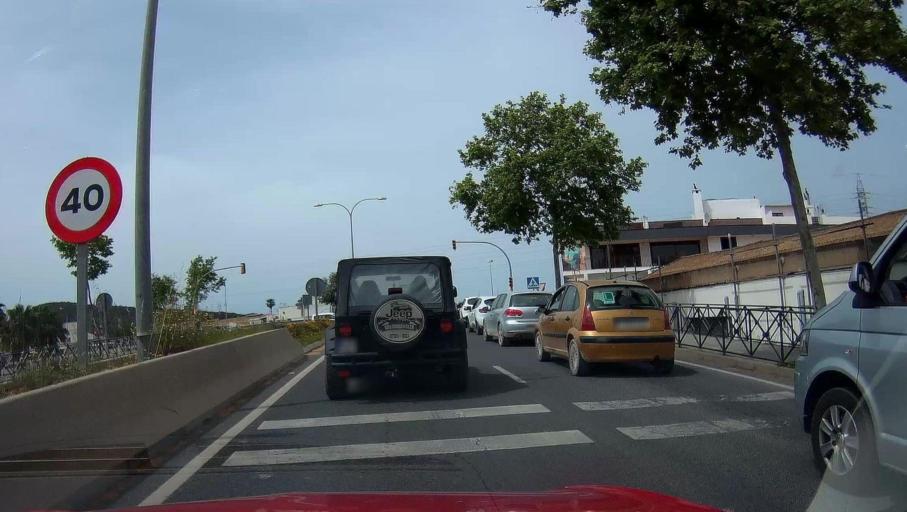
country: ES
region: Balearic Islands
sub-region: Illes Balears
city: Ibiza
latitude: 38.9194
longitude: 1.4261
